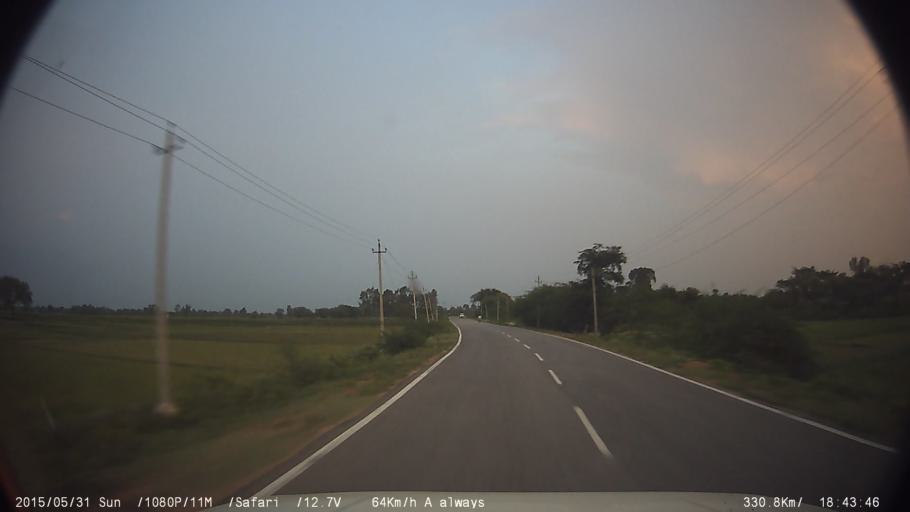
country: IN
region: Karnataka
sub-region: Mysore
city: Tirumakudal Narsipur
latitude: 12.1568
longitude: 76.8094
